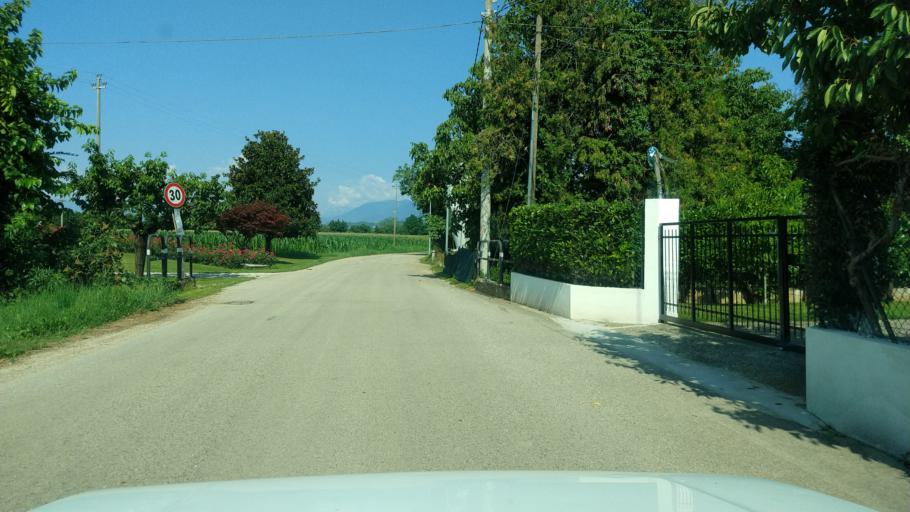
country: IT
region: Veneto
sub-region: Provincia di Vicenza
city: Schiavon
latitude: 45.7041
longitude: 11.6384
